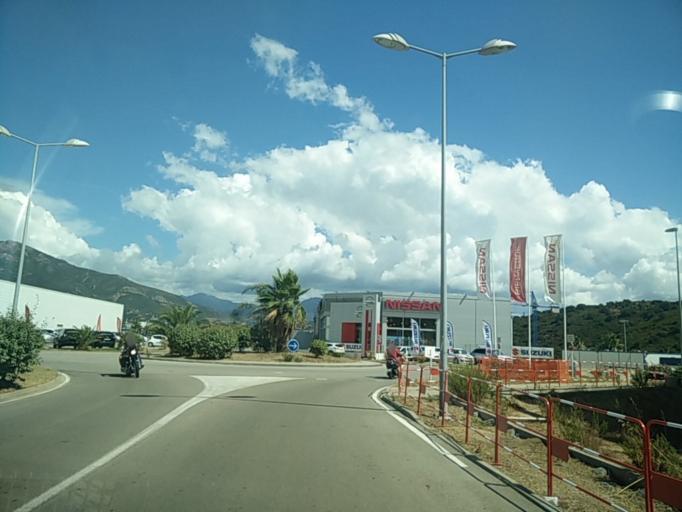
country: FR
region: Corsica
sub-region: Departement de la Corse-du-Sud
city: Afa
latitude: 41.9534
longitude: 8.7981
